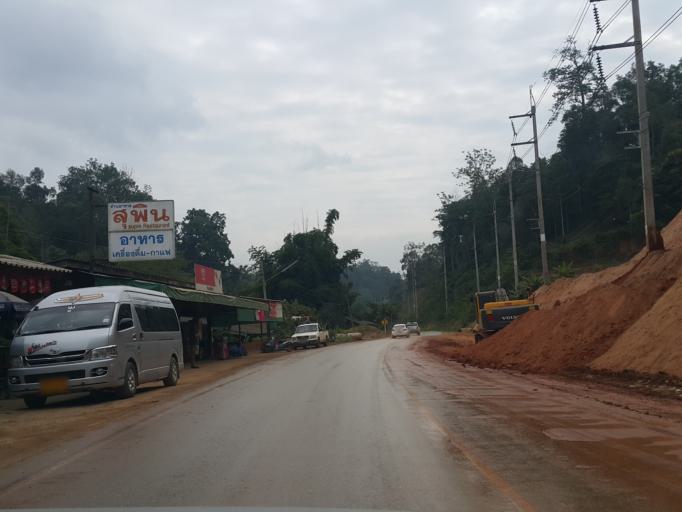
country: TH
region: Chiang Mai
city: Mae Taeng
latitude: 19.1611
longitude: 98.6905
